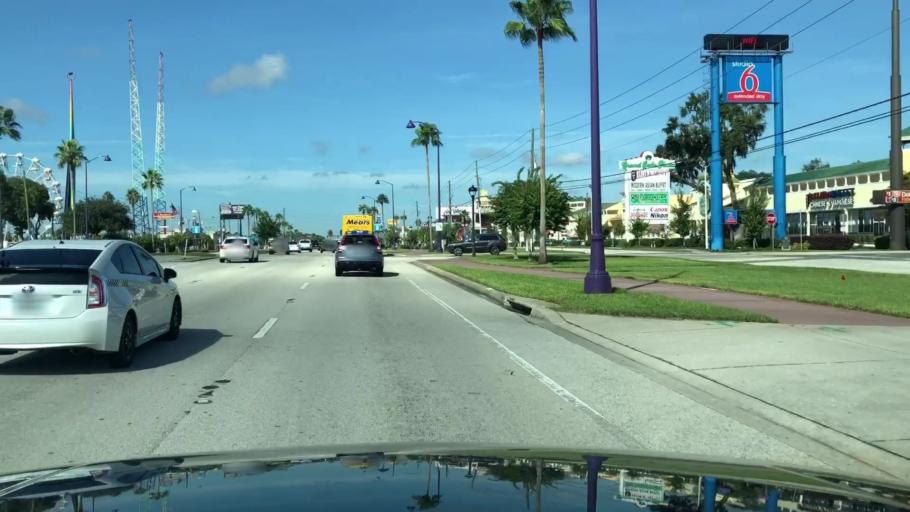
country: US
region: Florida
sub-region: Osceola County
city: Celebration
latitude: 28.3330
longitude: -81.5135
